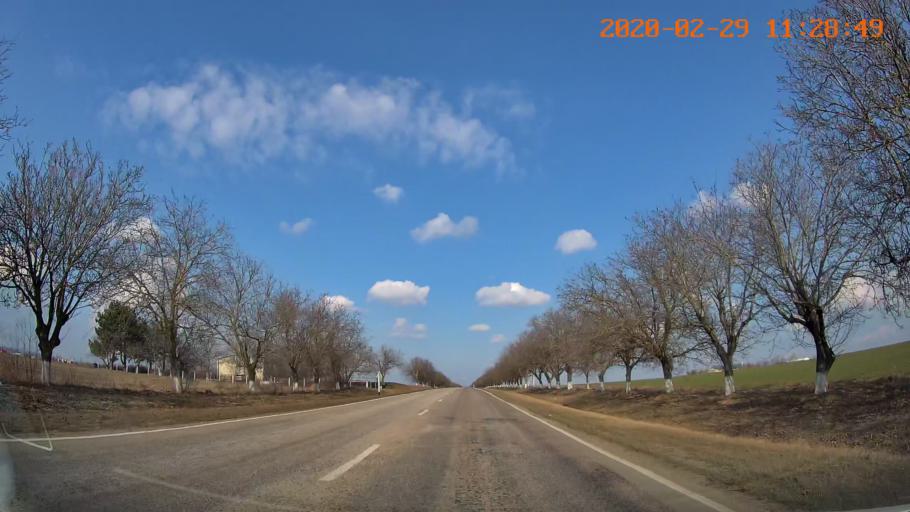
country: MD
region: Telenesti
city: Cocieri
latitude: 47.4849
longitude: 29.1308
